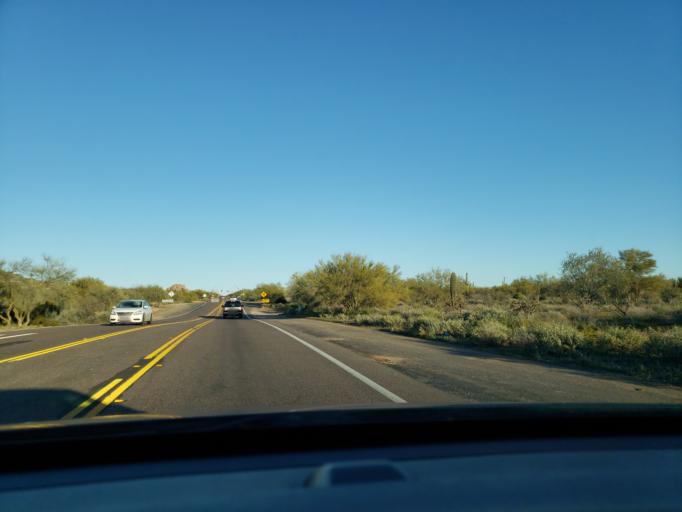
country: US
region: Arizona
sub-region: Maricopa County
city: Cave Creek
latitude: 33.7991
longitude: -111.9570
